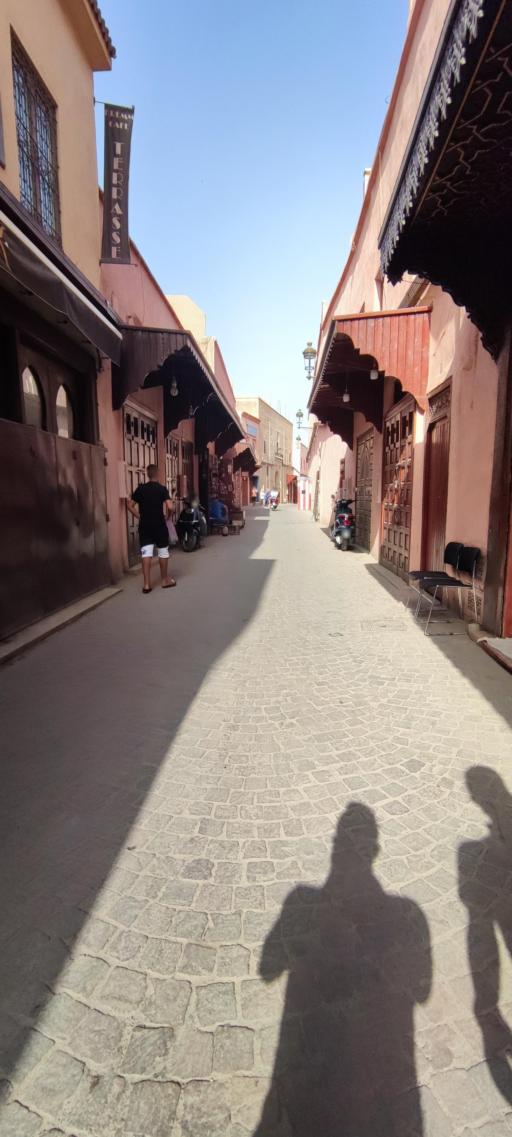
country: MA
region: Marrakech-Tensift-Al Haouz
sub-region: Marrakech
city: Marrakesh
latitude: 31.6316
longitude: -7.9912
